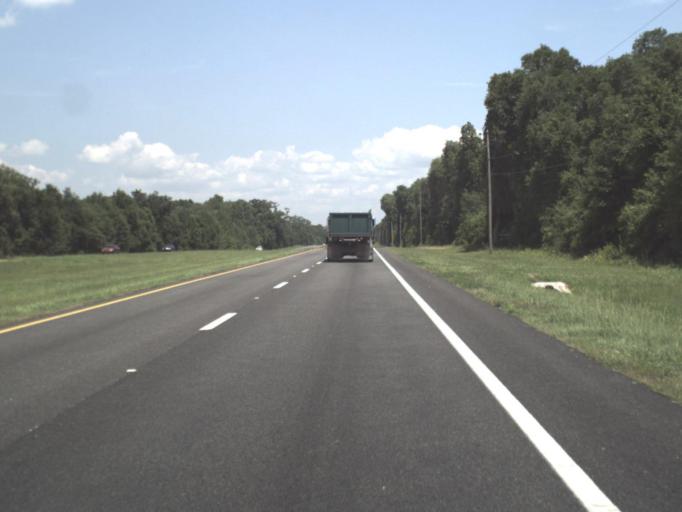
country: US
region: Florida
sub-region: Alachua County
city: Gainesville
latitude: 29.6082
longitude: -82.2337
